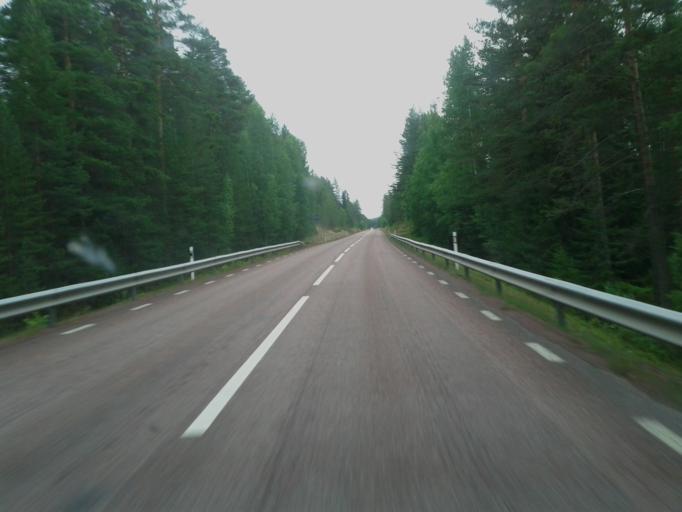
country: SE
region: Dalarna
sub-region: Mora Kommun
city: Mora
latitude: 61.1021
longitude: 14.2930
